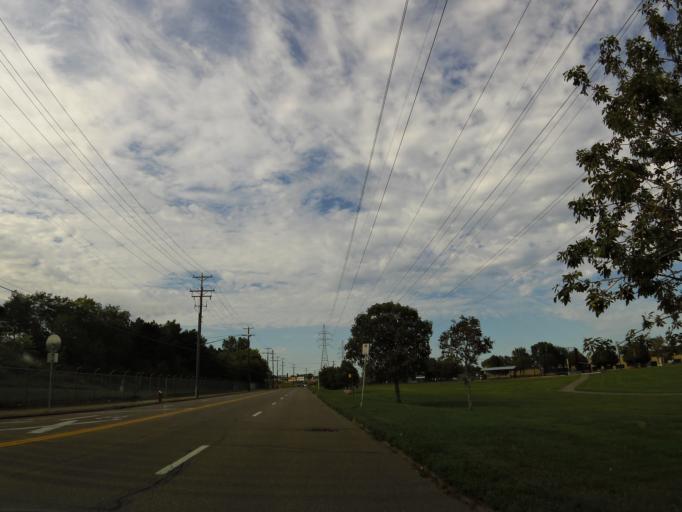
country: US
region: Minnesota
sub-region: Anoka County
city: Columbia Heights
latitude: 45.0254
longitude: -93.2746
